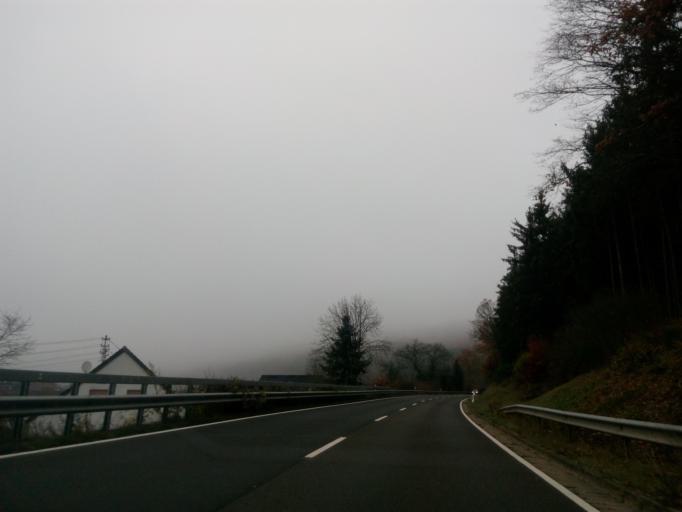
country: DE
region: Rheinland-Pfalz
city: Mittelreidenbach
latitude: 49.7250
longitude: 7.4443
